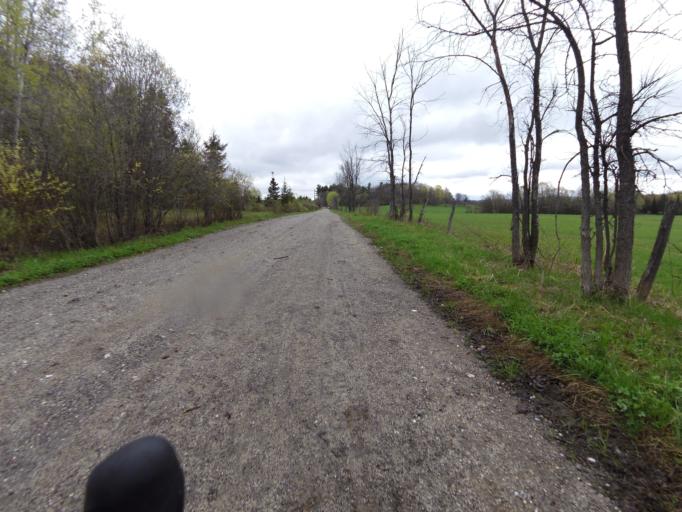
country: CA
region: Quebec
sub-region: Outaouais
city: Wakefield
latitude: 45.5904
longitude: -75.9027
